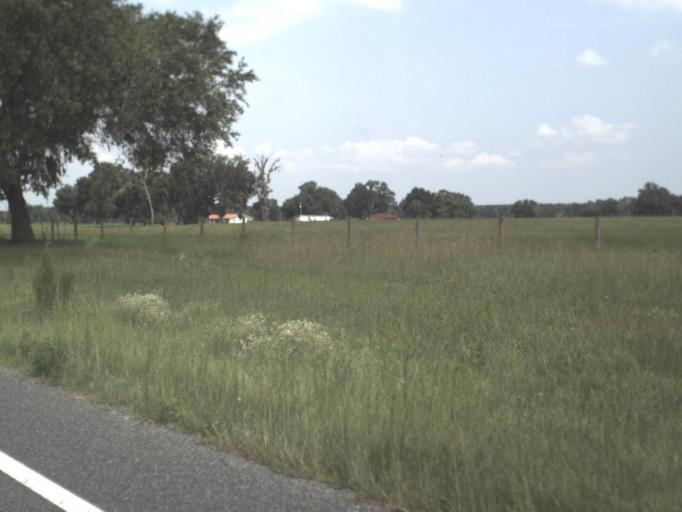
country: US
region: Florida
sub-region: Levy County
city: Bronson
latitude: 29.4752
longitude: -82.7487
